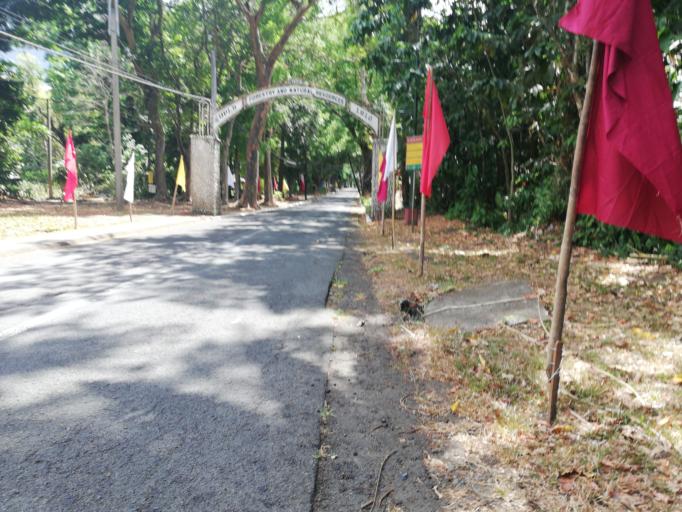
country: PH
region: Calabarzon
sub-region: Province of Laguna
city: Los Banos
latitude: 14.1577
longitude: 121.2365
